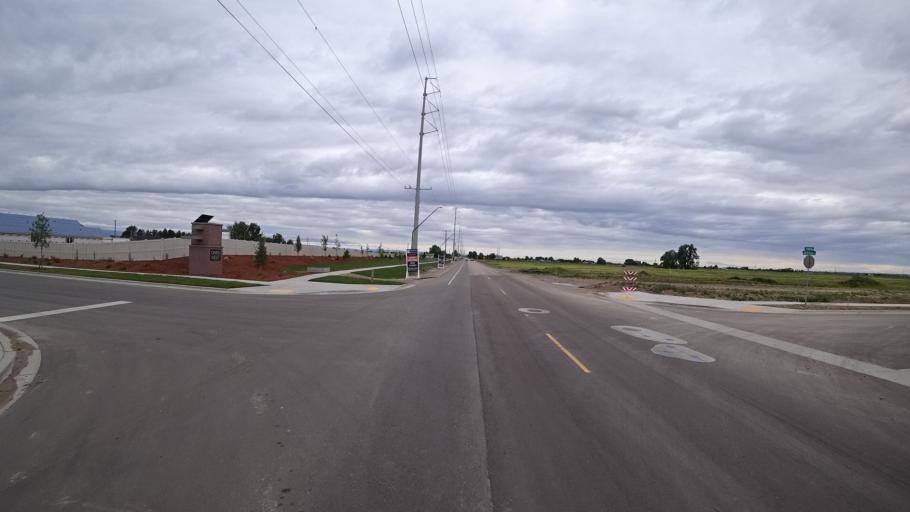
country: US
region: Idaho
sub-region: Ada County
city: Star
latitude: 43.6485
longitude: -116.4700
